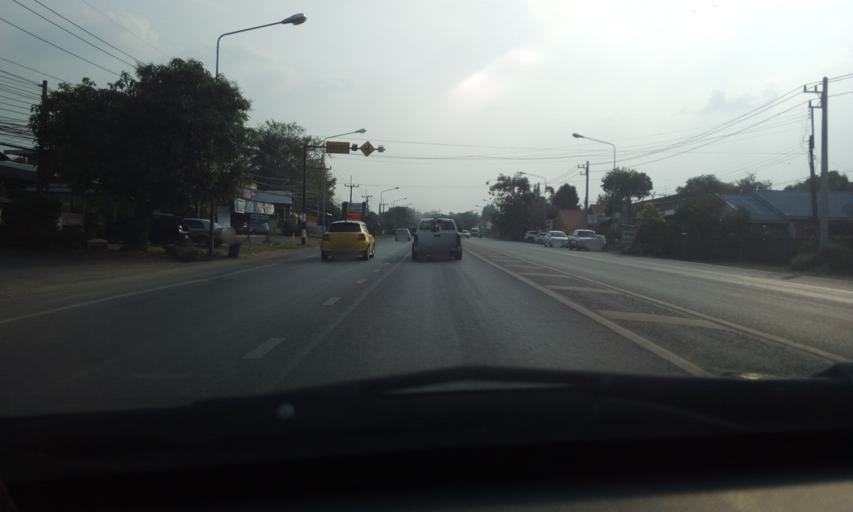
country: TH
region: Nakhon Nayok
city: Nakhon Nayok
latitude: 14.2138
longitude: 101.2248
